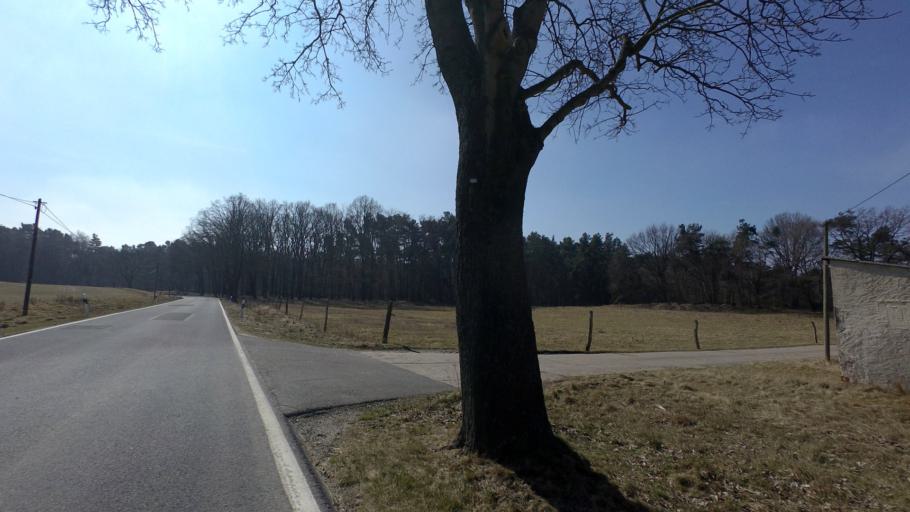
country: DE
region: Brandenburg
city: Wiesenburg
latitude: 52.0346
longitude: 12.5191
